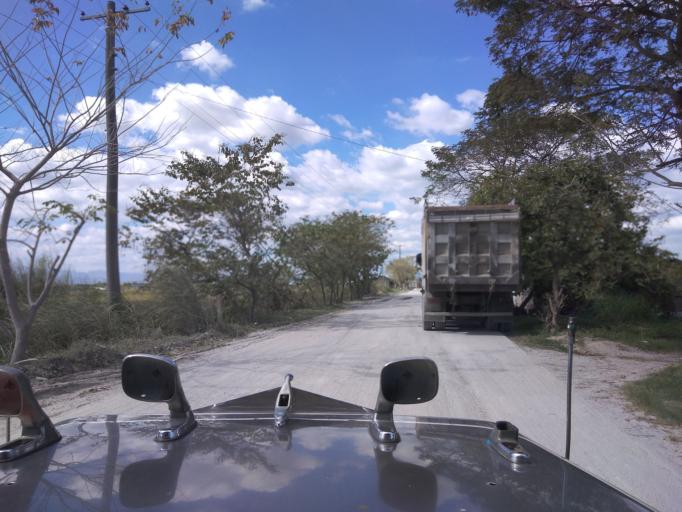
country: PH
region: Central Luzon
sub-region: Province of Pampanga
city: Magliman
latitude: 15.0397
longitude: 120.6310
